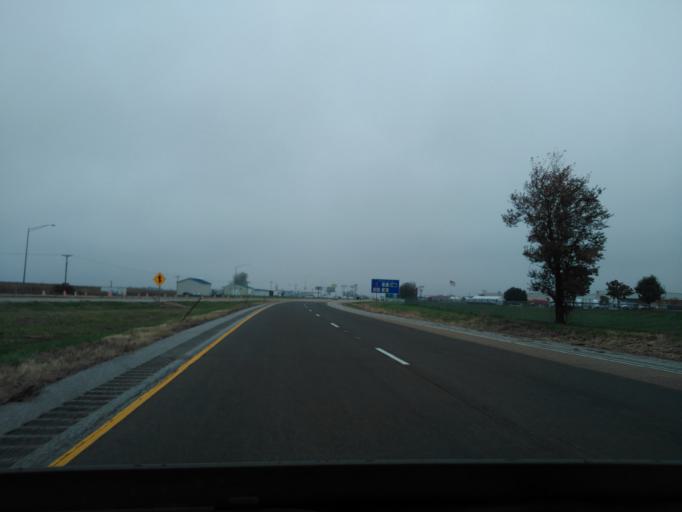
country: US
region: Illinois
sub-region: Madison County
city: Troy
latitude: 38.7446
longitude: -89.9098
